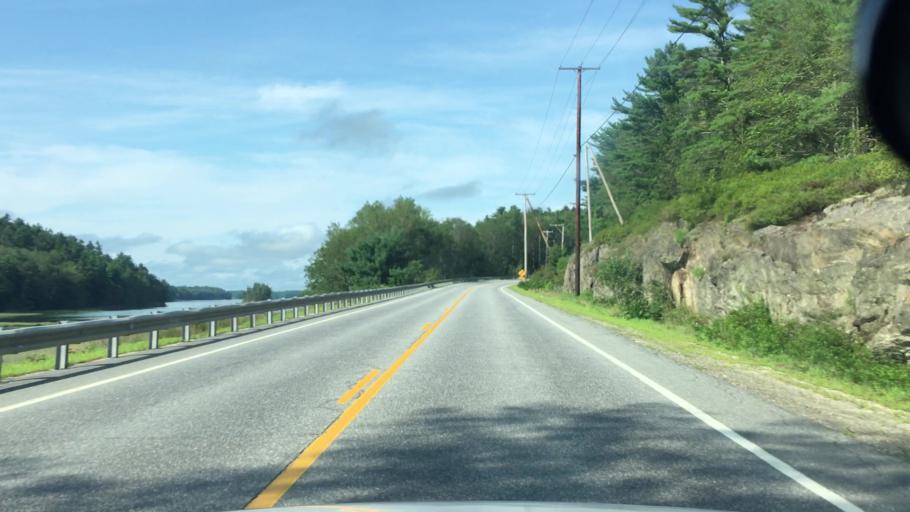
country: US
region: Maine
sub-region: Cumberland County
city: Harpswell Center
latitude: 43.8066
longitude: -69.9318
